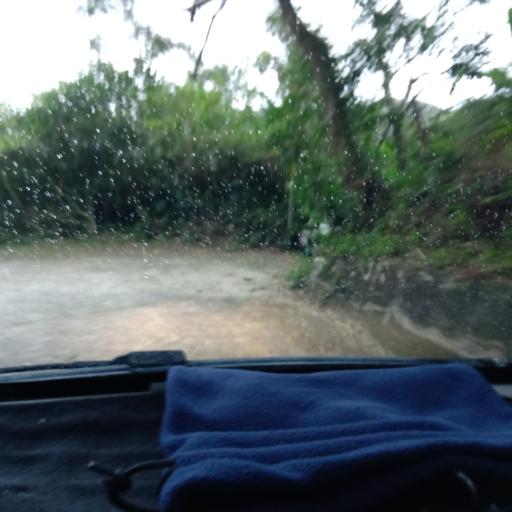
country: TW
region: Taiwan
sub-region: Yilan
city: Yilan
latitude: 24.8077
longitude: 121.6960
